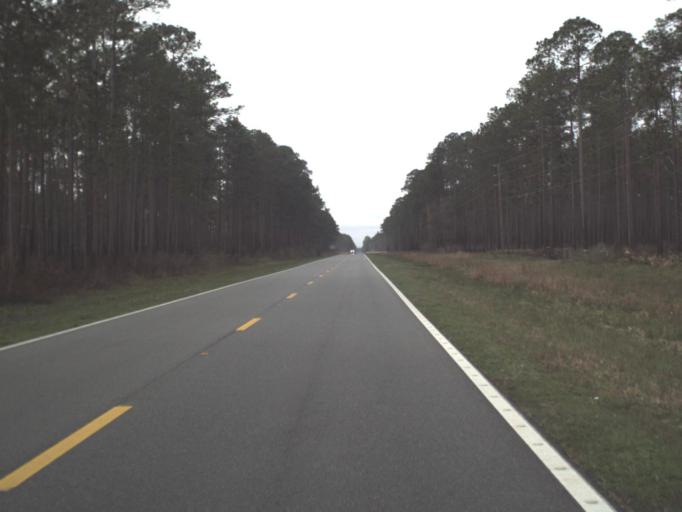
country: US
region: Florida
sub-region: Gulf County
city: Wewahitchka
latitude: 30.1645
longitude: -84.9553
